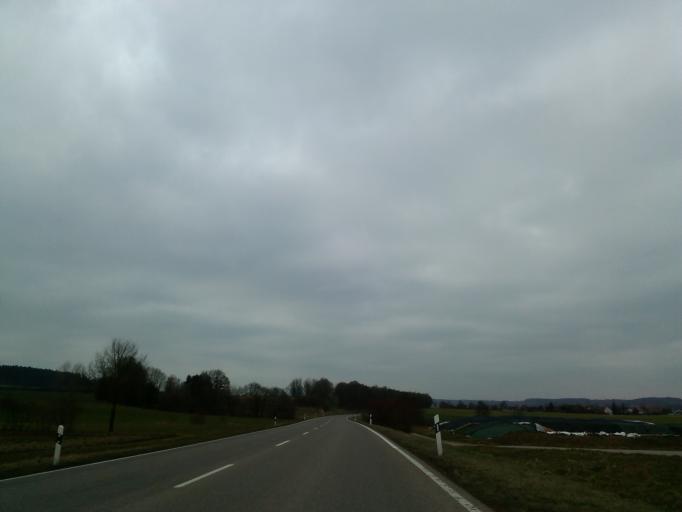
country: DE
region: Bavaria
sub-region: Swabia
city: Ziemetshausen
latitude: 48.3030
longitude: 10.5660
